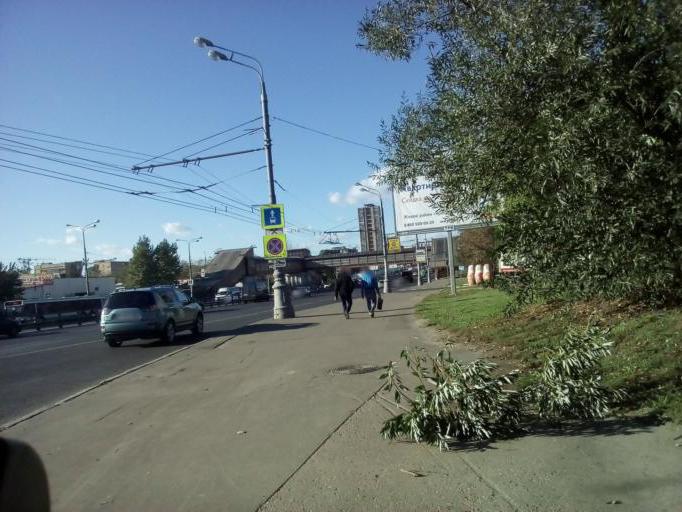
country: RU
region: Moscow
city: Likhobory
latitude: 55.8499
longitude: 37.5670
